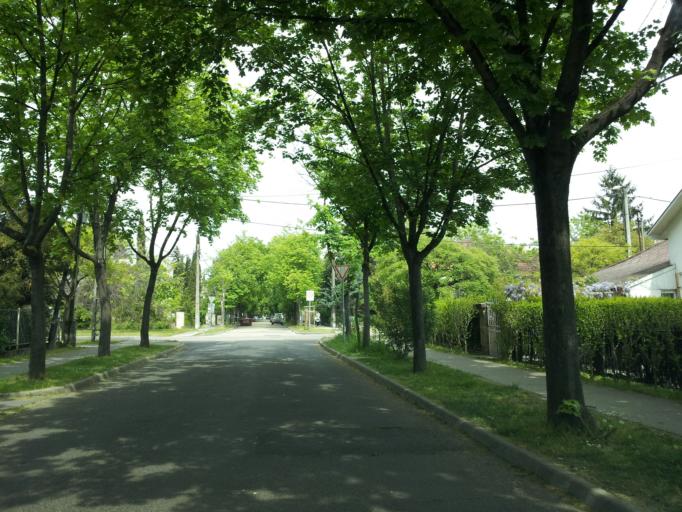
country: HU
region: Budapest
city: Budapest IV. keruelet
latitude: 47.5722
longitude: 19.0596
